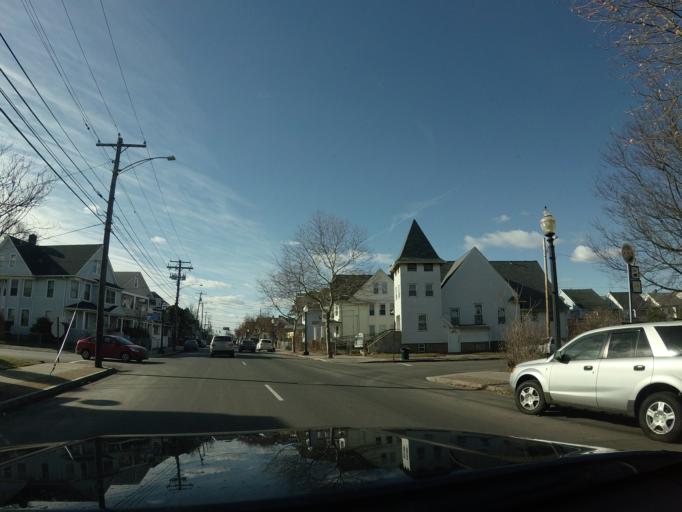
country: US
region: Connecticut
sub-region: Fairfield County
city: Stratford
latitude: 41.1799
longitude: -73.1669
